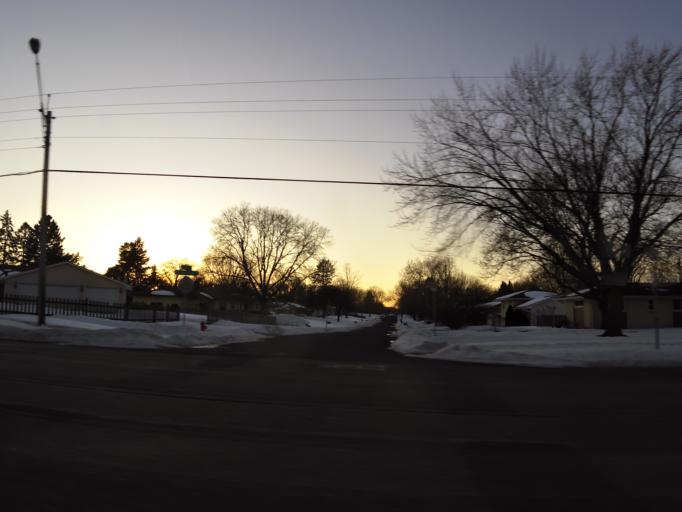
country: US
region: Minnesota
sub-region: Ramsey County
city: White Bear Lake
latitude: 45.0611
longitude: -93.0154
